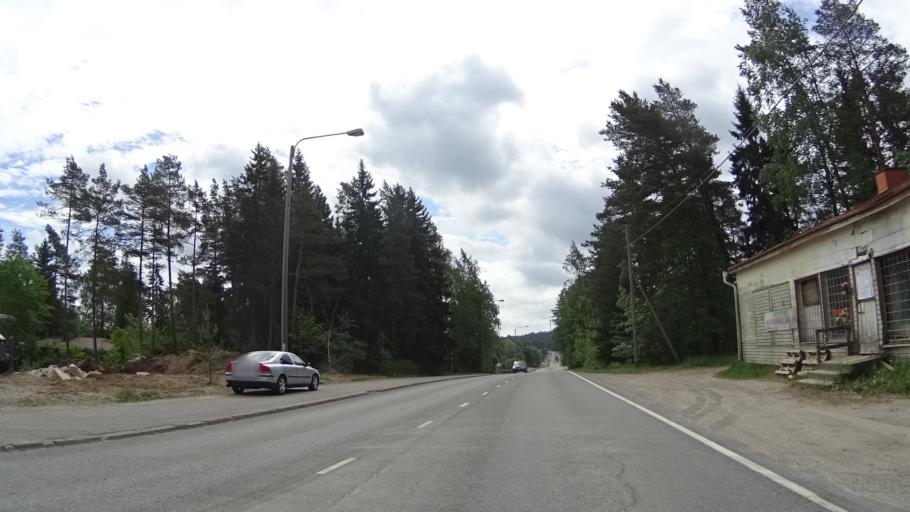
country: FI
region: Uusimaa
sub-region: Helsinki
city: Kirkkonummi
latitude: 60.2785
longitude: 24.4130
